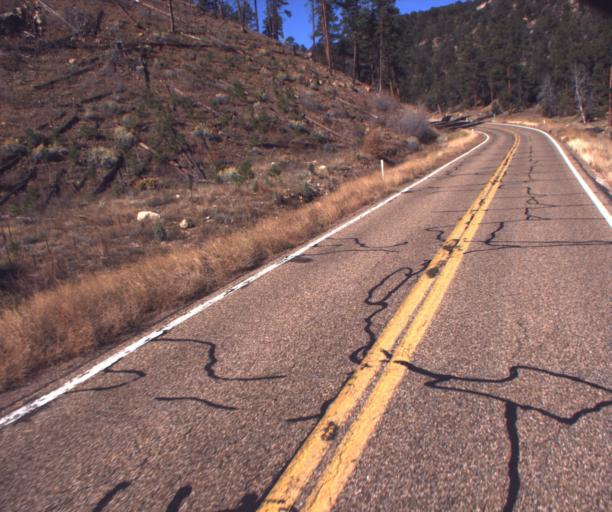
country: US
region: Arizona
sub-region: Coconino County
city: Fredonia
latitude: 36.7349
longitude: -112.1402
